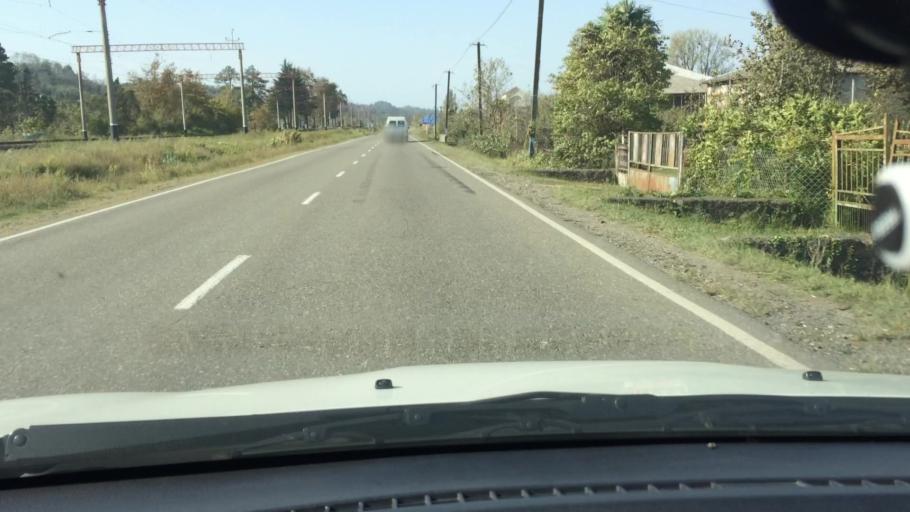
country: GE
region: Guria
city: Lanchkhuti
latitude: 42.0768
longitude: 41.9117
